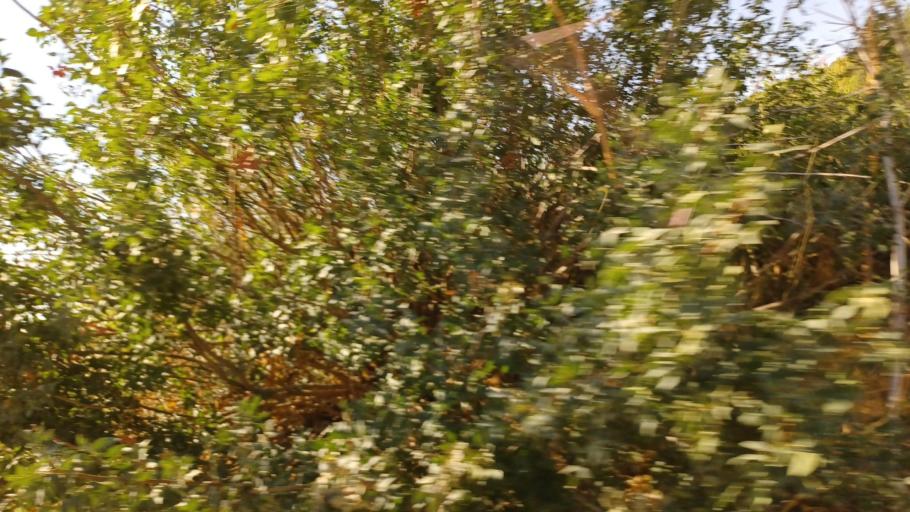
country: CY
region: Pafos
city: Polis
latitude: 34.9649
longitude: 32.4952
